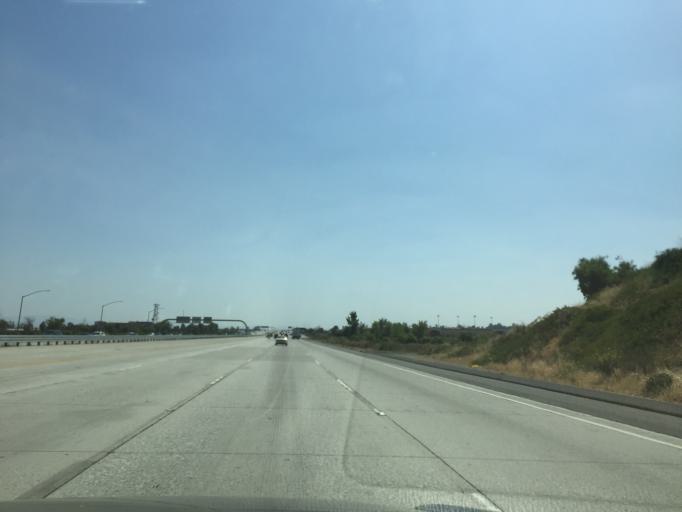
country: US
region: California
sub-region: San Bernardino County
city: Fontana
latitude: 34.1348
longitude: -117.4981
